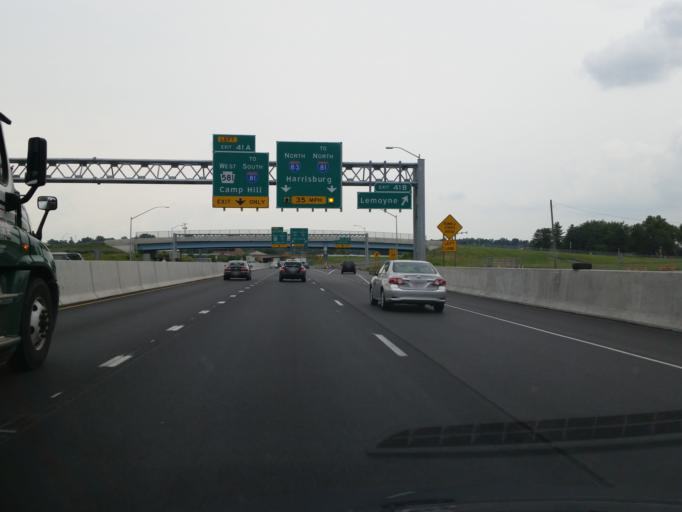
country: US
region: Pennsylvania
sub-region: Cumberland County
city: Lemoyne
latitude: 40.2348
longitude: -76.8928
